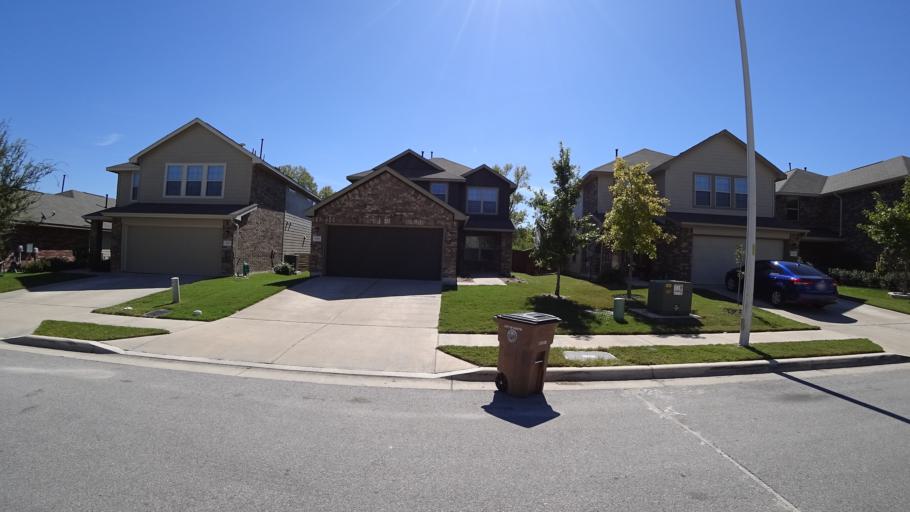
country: US
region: Texas
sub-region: Travis County
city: Austin
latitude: 30.1977
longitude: -97.7013
